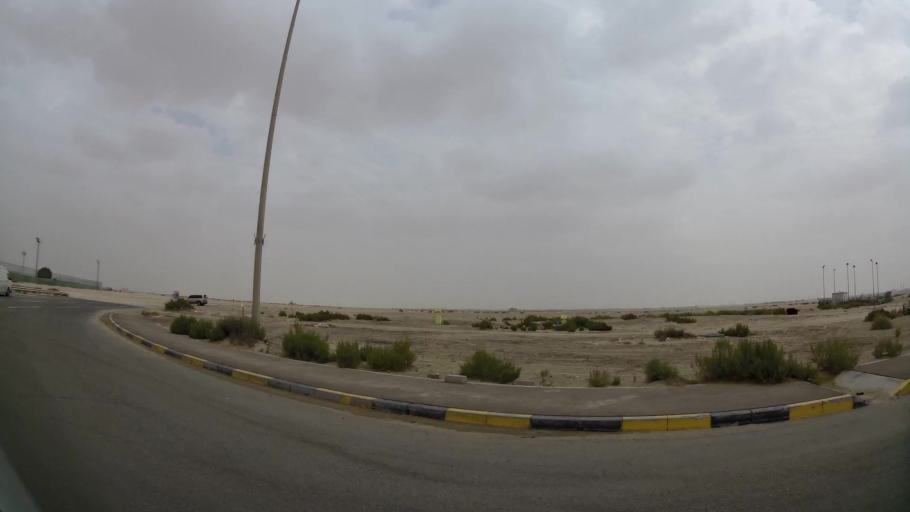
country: AE
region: Abu Dhabi
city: Abu Dhabi
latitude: 24.3788
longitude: 54.6672
